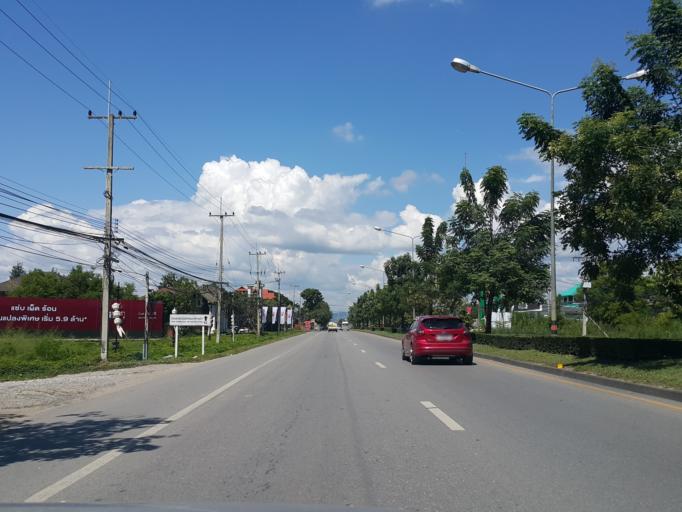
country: TH
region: Chiang Mai
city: San Sai
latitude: 18.8388
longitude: 99.0130
